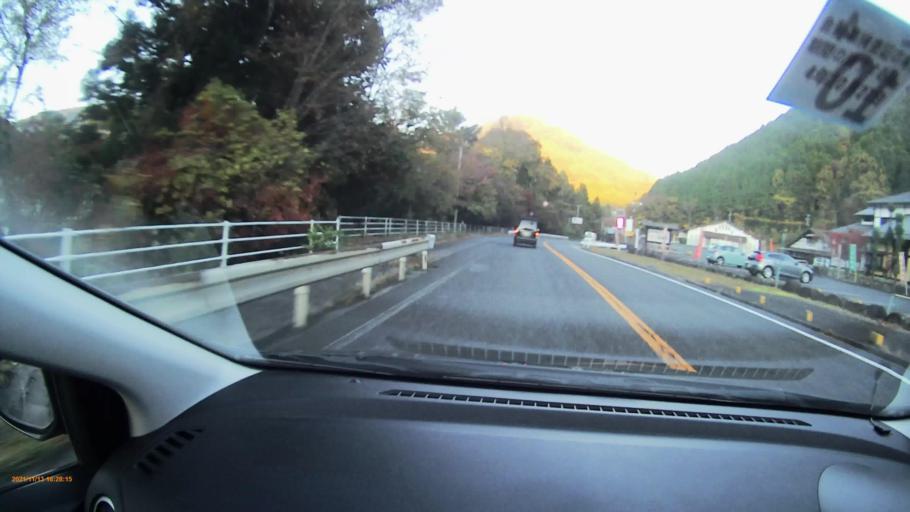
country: JP
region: Gifu
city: Nakatsugawa
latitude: 35.5857
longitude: 137.5443
